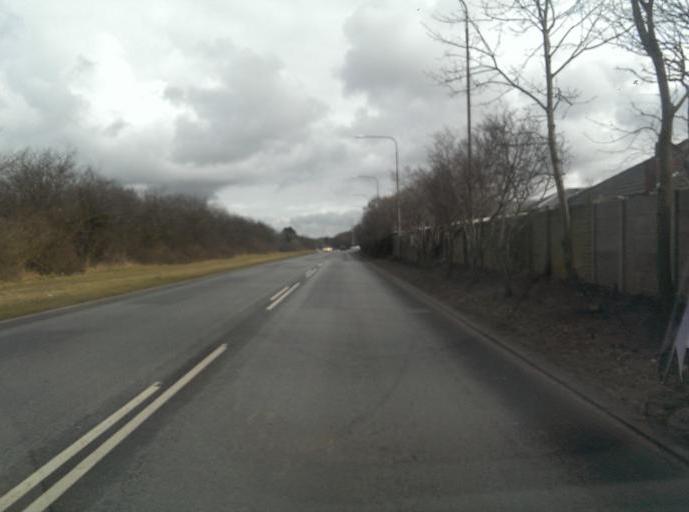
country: DK
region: South Denmark
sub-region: Esbjerg Kommune
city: Esbjerg
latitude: 55.5039
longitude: 8.4187
